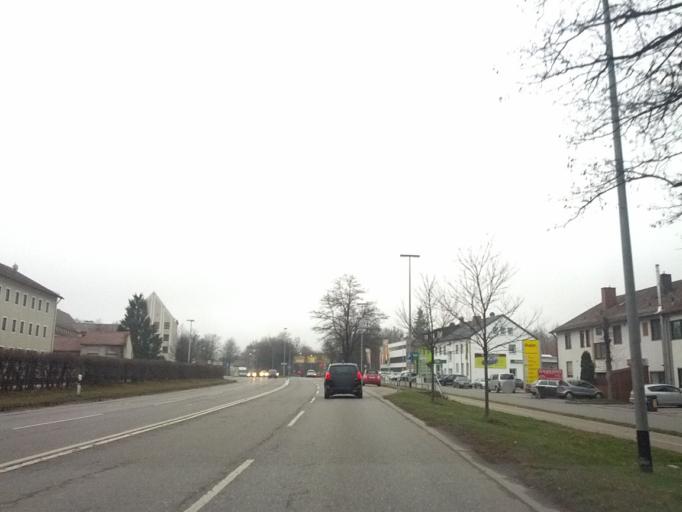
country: DE
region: Bavaria
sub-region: Swabia
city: Kempten (Allgaeu)
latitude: 47.7370
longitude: 10.3235
